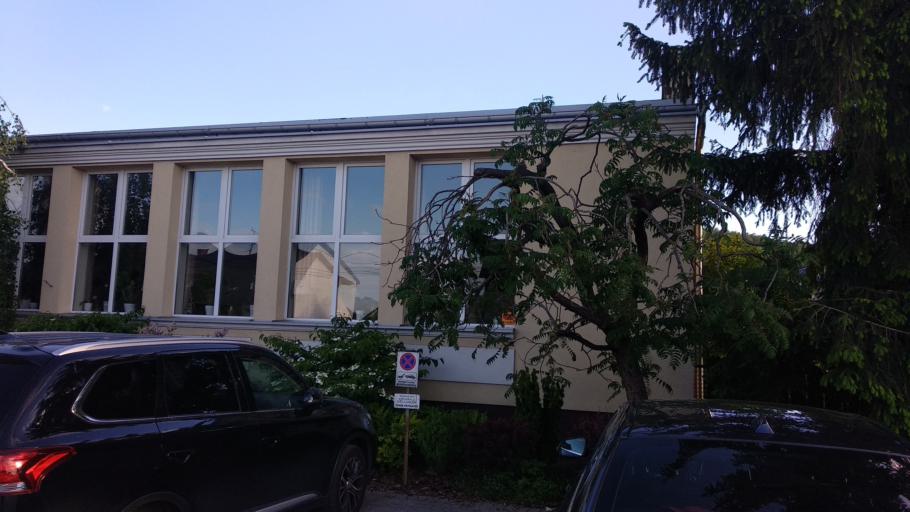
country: PL
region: Swietokrzyskie
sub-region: Powiat kielecki
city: Checiny
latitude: 50.8026
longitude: 20.4623
